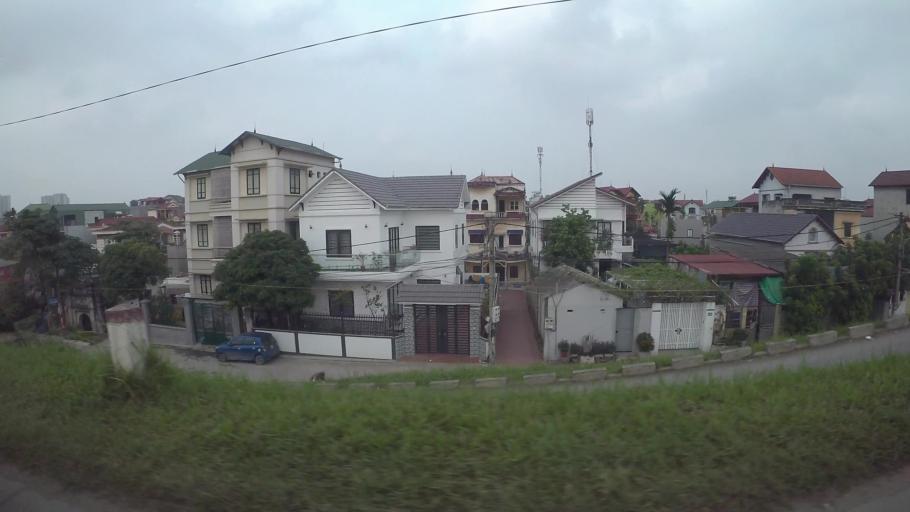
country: VN
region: Ha Noi
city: Trau Quy
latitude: 21.0082
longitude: 105.9067
